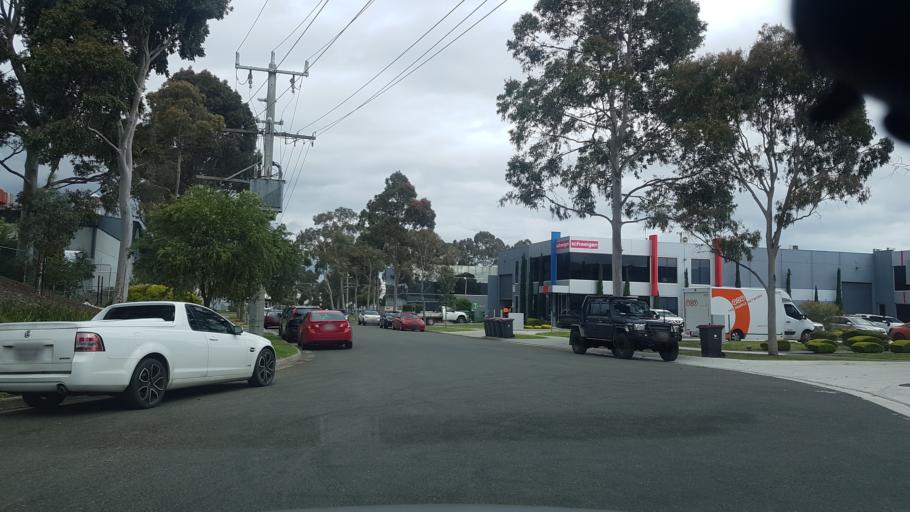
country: AU
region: Victoria
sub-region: Monash
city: Notting Hill
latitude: -37.9217
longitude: 145.1500
